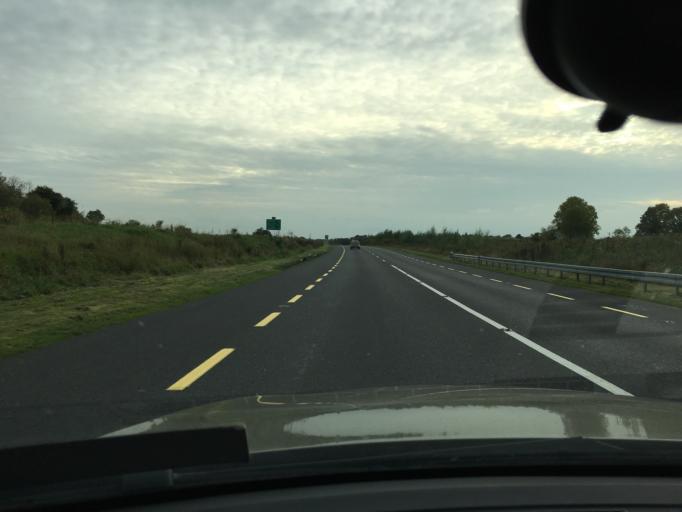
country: IE
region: Leinster
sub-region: An Longfort
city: Longford
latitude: 53.7436
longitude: -7.8093
